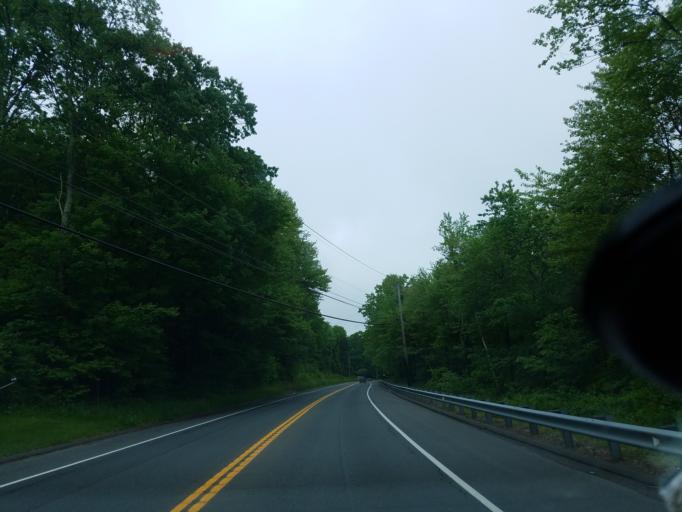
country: US
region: Connecticut
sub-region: Litchfield County
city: Northwest Harwinton
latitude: 41.7924
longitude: -73.0775
